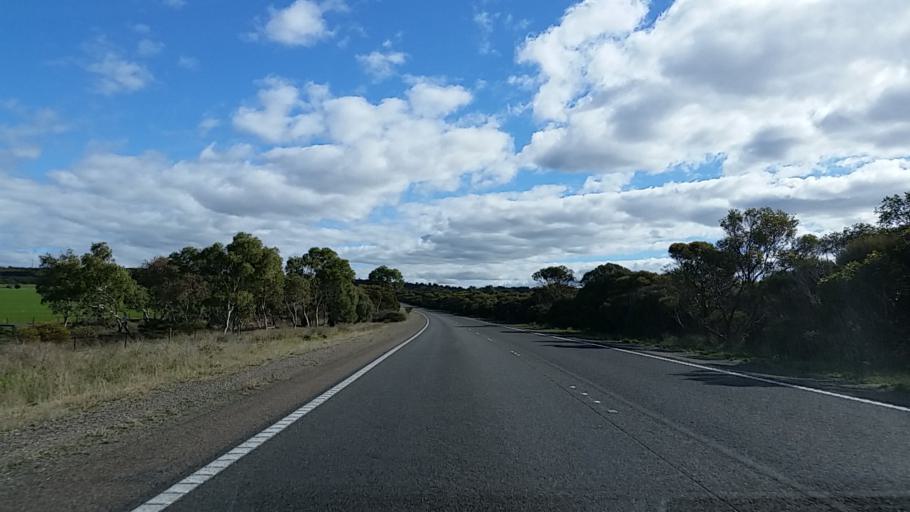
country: AU
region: South Australia
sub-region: Murray Bridge
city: Murray Bridge
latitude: -35.1435
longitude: 139.2455
